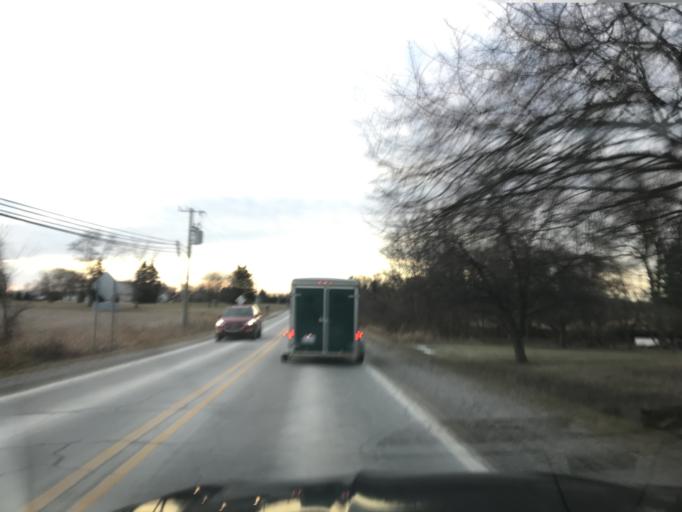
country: US
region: Michigan
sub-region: Macomb County
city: Armada
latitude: 42.8640
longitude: -82.8850
